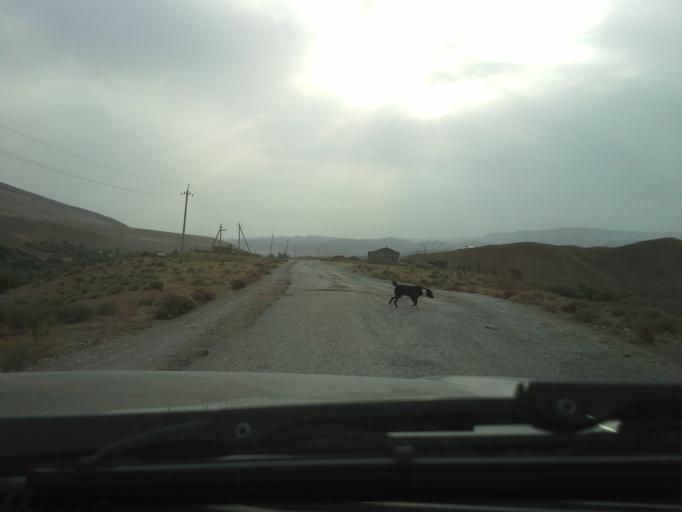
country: UZ
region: Qashqadaryo
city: Qorashina
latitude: 37.9359
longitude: 66.5137
